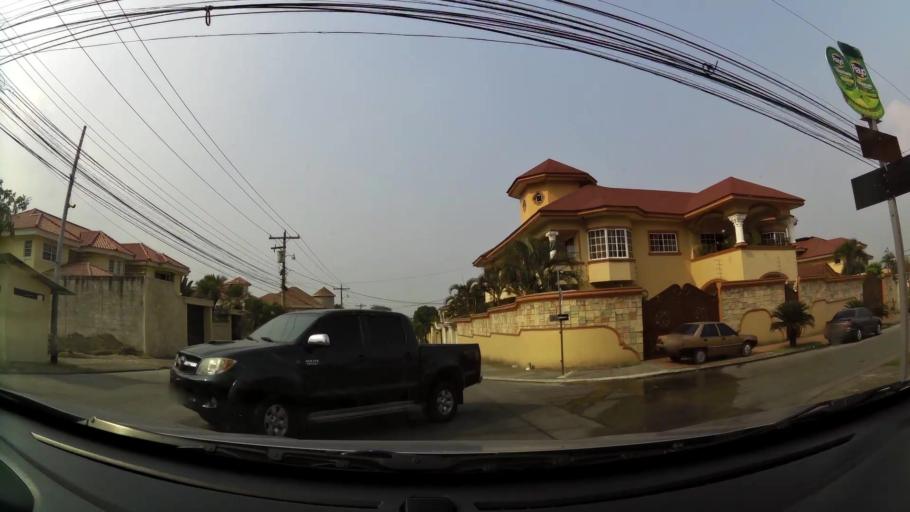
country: HN
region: Cortes
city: El Zapotal del Norte
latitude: 15.5123
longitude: -88.0428
